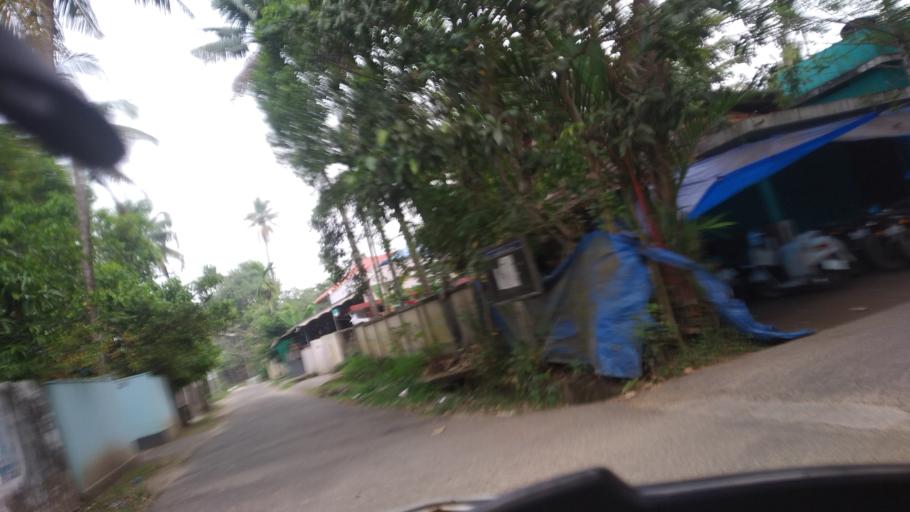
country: IN
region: Kerala
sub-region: Thrissur District
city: Kodungallur
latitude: 10.1454
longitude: 76.2412
